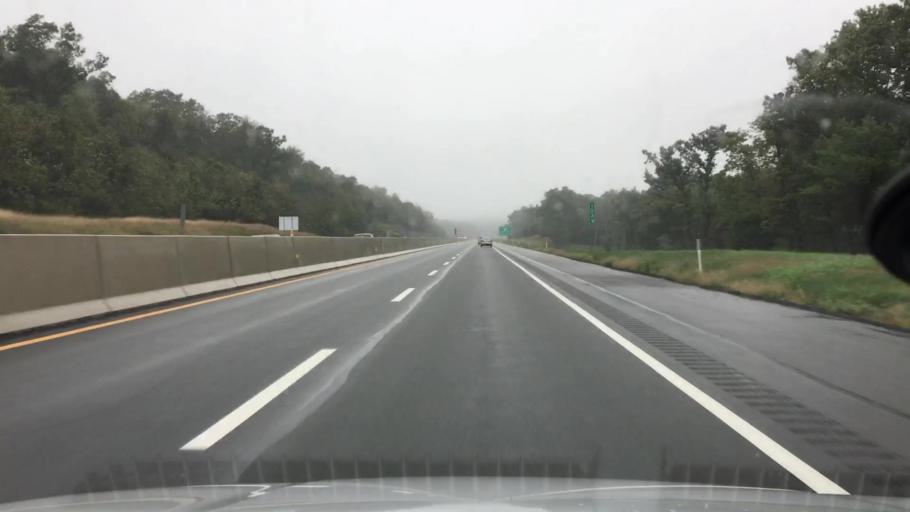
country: US
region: Pennsylvania
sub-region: Luzerne County
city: Mountain Top
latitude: 41.1790
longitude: -75.7842
